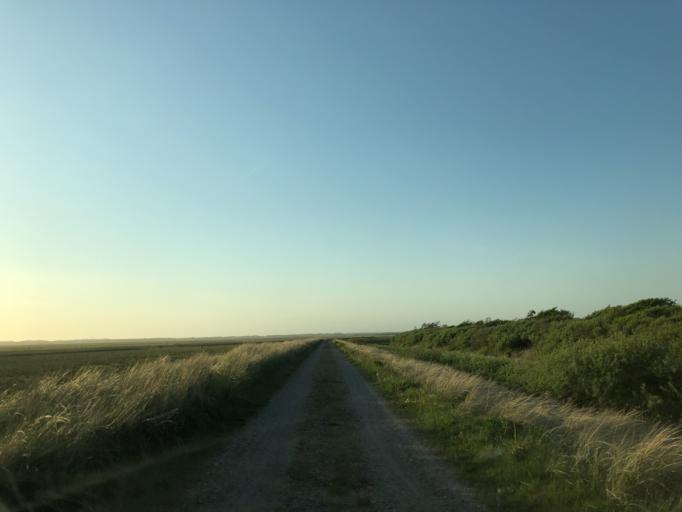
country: DK
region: Central Jutland
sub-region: Ringkobing-Skjern Kommune
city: Ringkobing
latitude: 56.2292
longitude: 8.1666
